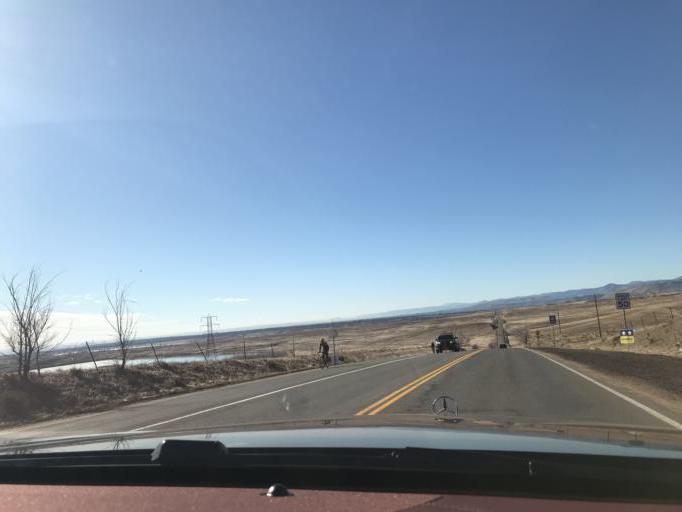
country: US
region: Colorado
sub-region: Boulder County
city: Superior
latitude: 39.9101
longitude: -105.1658
